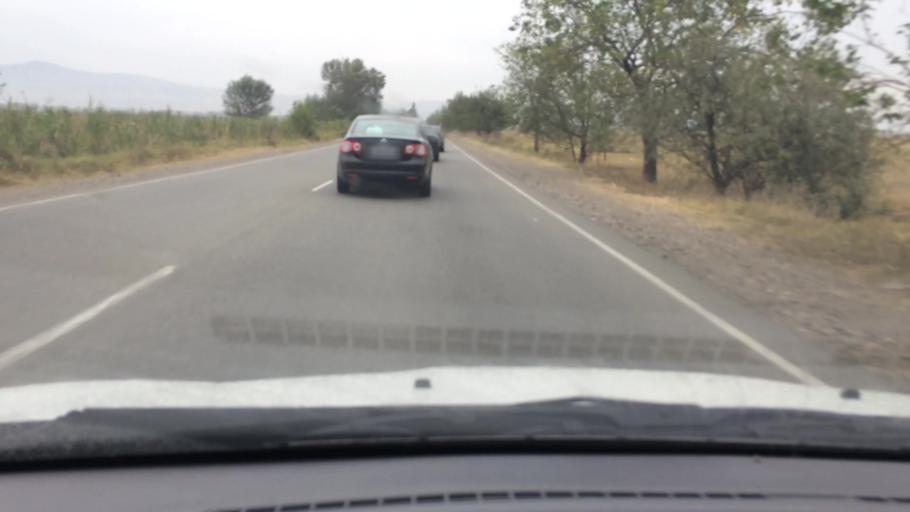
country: GE
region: Kvemo Kartli
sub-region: Marneuli
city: Marneuli
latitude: 41.5449
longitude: 44.7767
